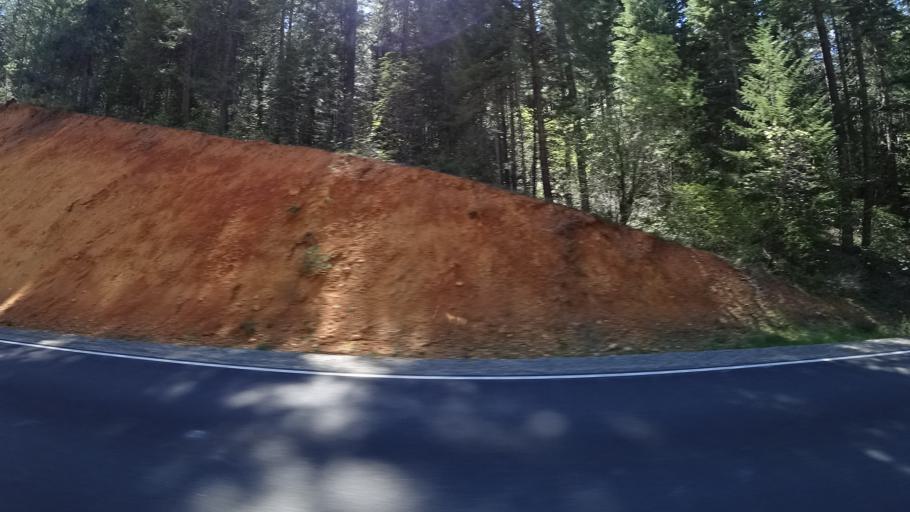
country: US
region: California
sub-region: Trinity County
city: Lewiston
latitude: 40.9033
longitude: -122.7883
